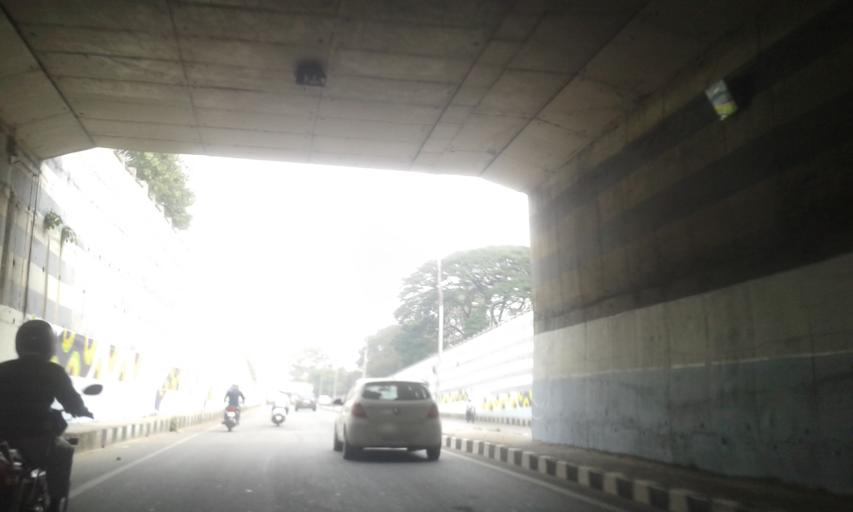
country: IN
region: Karnataka
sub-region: Bangalore Urban
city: Bangalore
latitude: 12.9371
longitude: 77.6016
